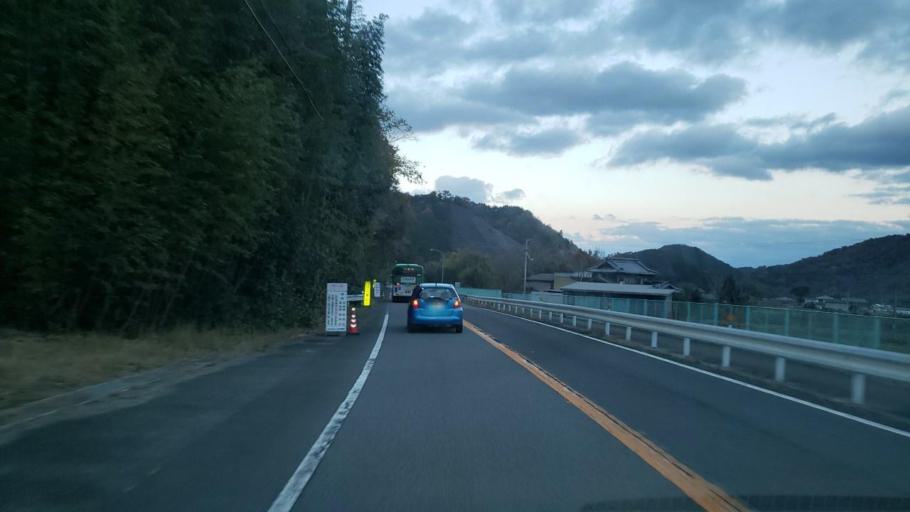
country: JP
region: Tokushima
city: Kamojimacho-jogejima
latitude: 34.2148
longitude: 134.3327
